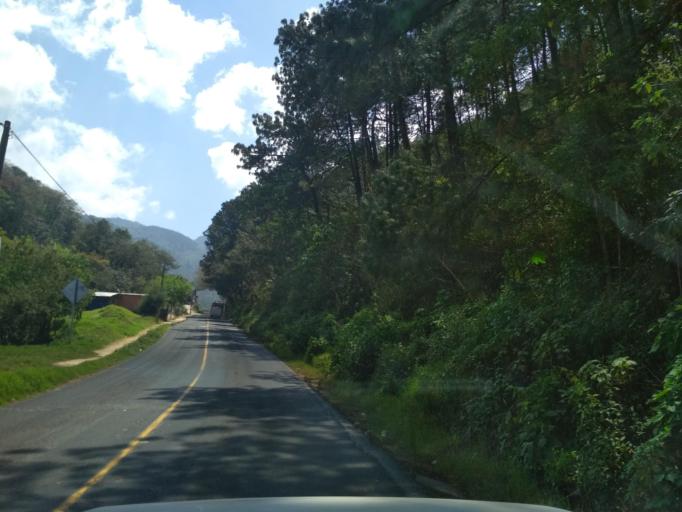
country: MX
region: Veracruz
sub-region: Tlilapan
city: Tonalixco
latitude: 18.7788
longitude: -97.0838
